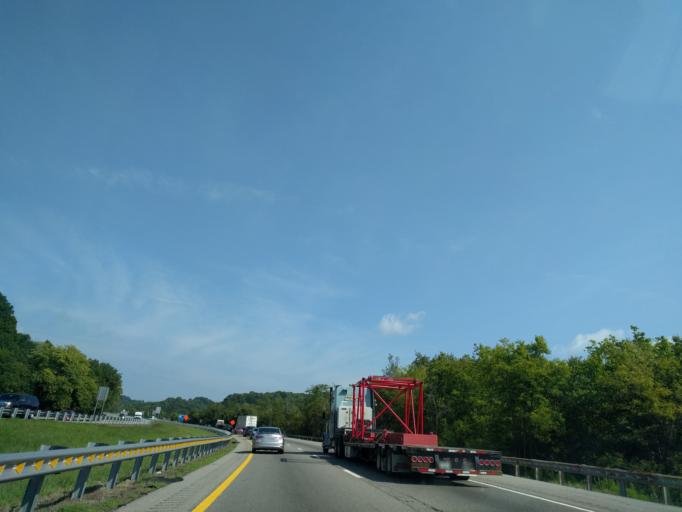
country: US
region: Tennessee
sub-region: Sumner County
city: Millersville
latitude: 36.3973
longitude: -86.7172
